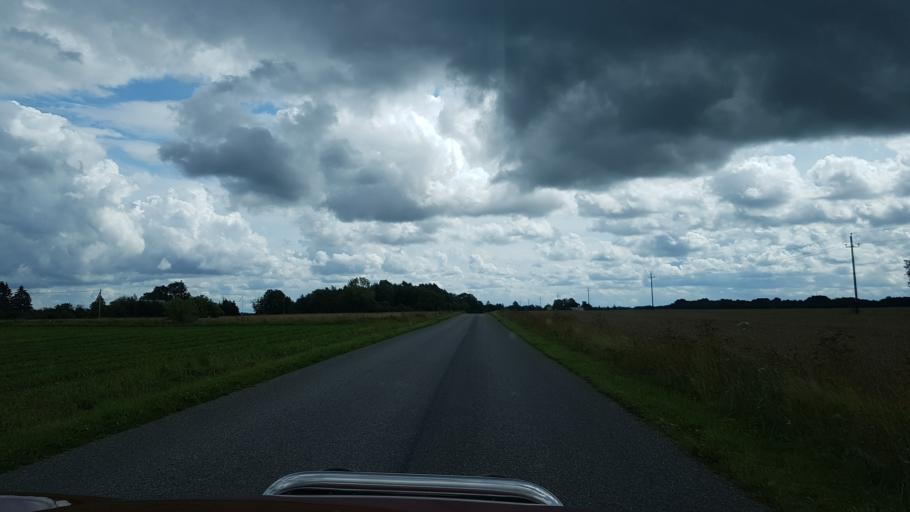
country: EE
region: Laeaene
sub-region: Lihula vald
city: Lihula
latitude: 58.7151
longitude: 23.9973
